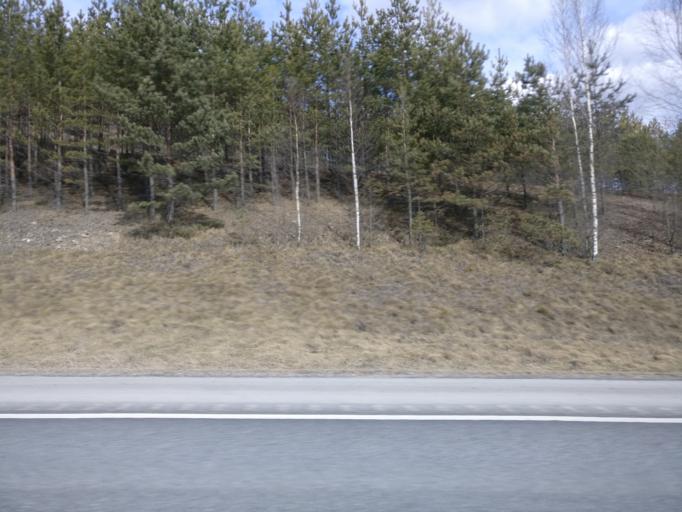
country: FI
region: Haeme
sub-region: Haemeenlinna
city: Parola
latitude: 61.0608
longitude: 24.3344
